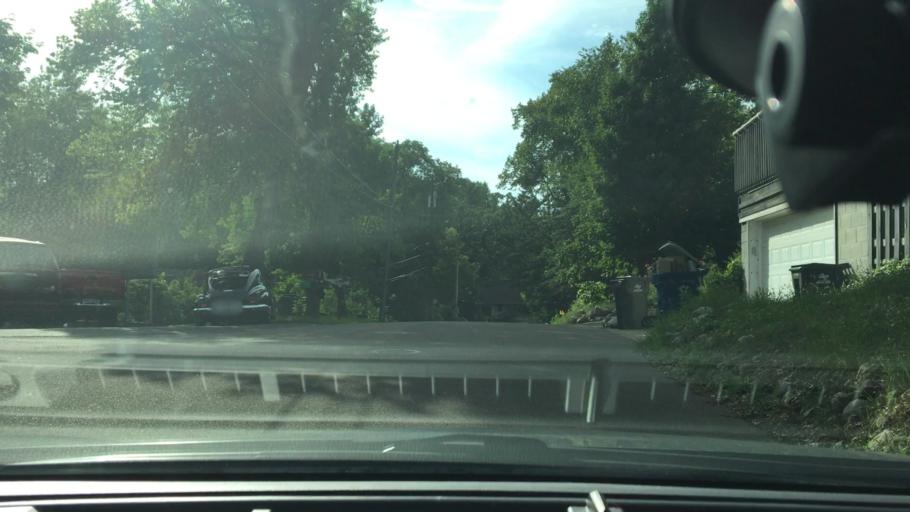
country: US
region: Minnesota
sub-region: Hennepin County
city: Plymouth
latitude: 45.0058
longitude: -93.4357
